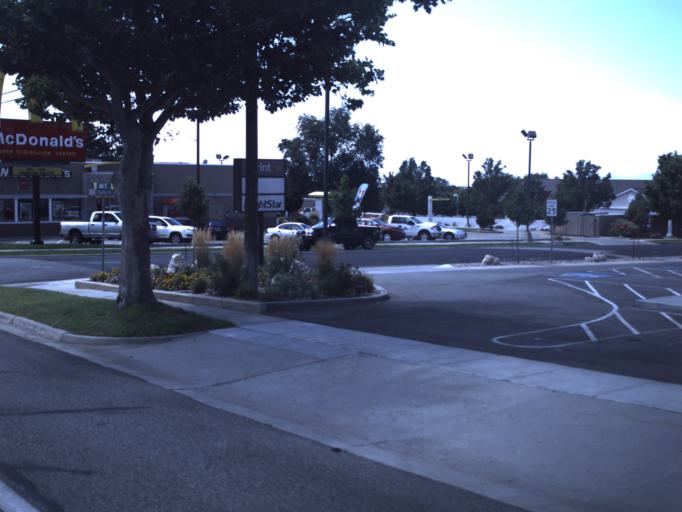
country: US
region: Utah
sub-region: Box Elder County
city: Brigham City
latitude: 41.4929
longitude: -112.0162
